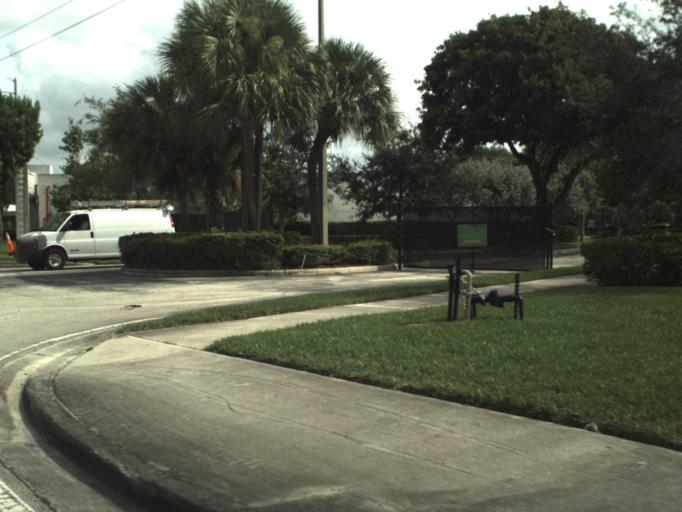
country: US
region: Florida
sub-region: Palm Beach County
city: Delray Beach
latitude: 26.4528
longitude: -80.0932
